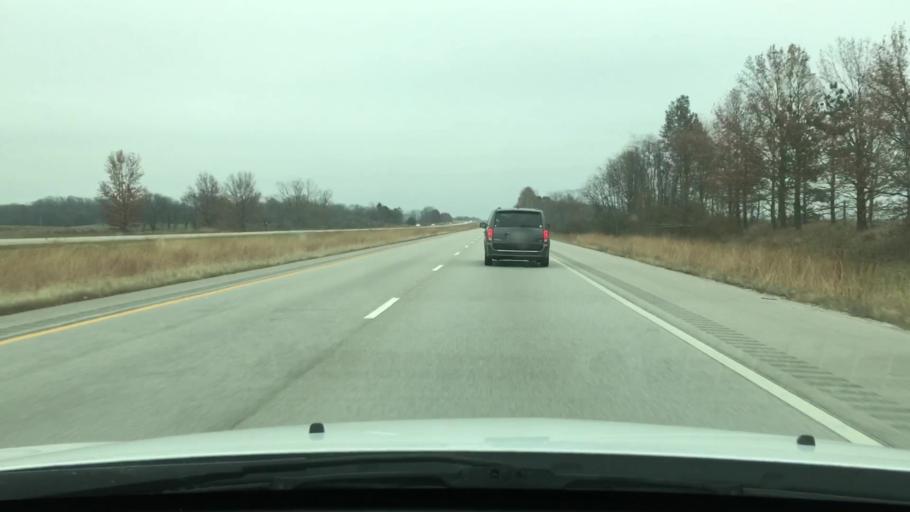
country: US
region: Illinois
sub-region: Sangamon County
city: New Berlin
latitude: 39.7398
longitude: -89.9666
